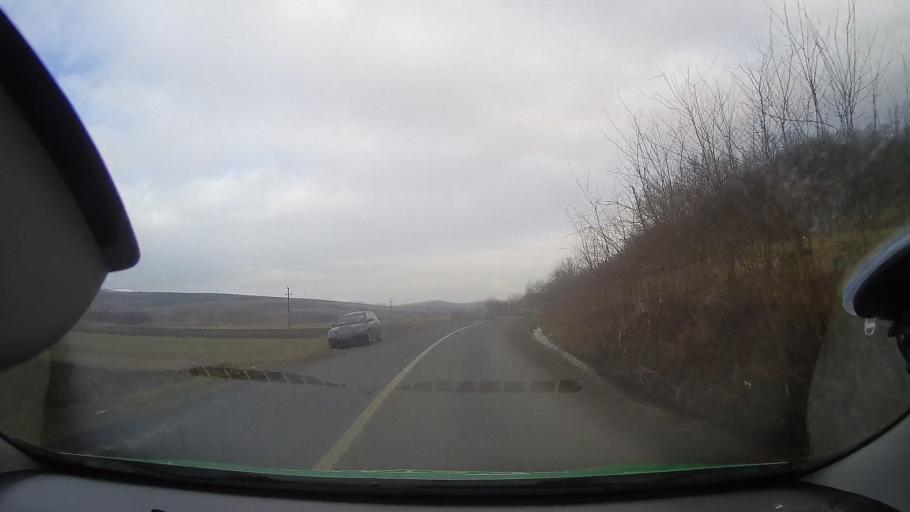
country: RO
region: Mures
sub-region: Comuna Ludus
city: Gheja
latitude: 46.4073
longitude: 24.0680
